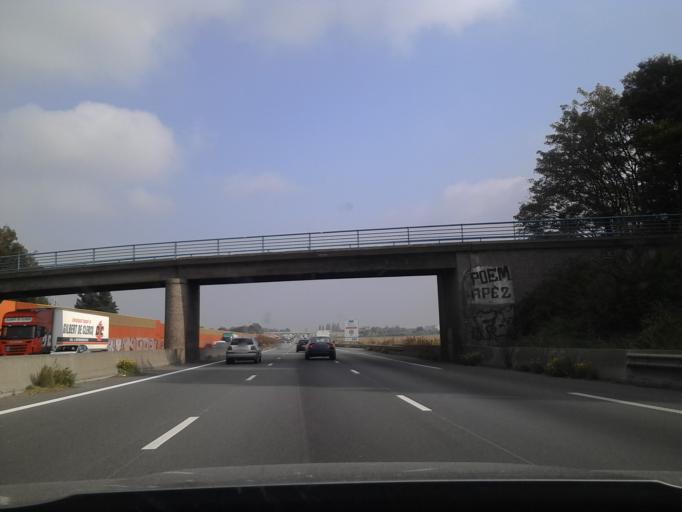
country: FR
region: Nord-Pas-de-Calais
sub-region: Departement du Nord
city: Vendeville
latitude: 50.5715
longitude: 3.0791
